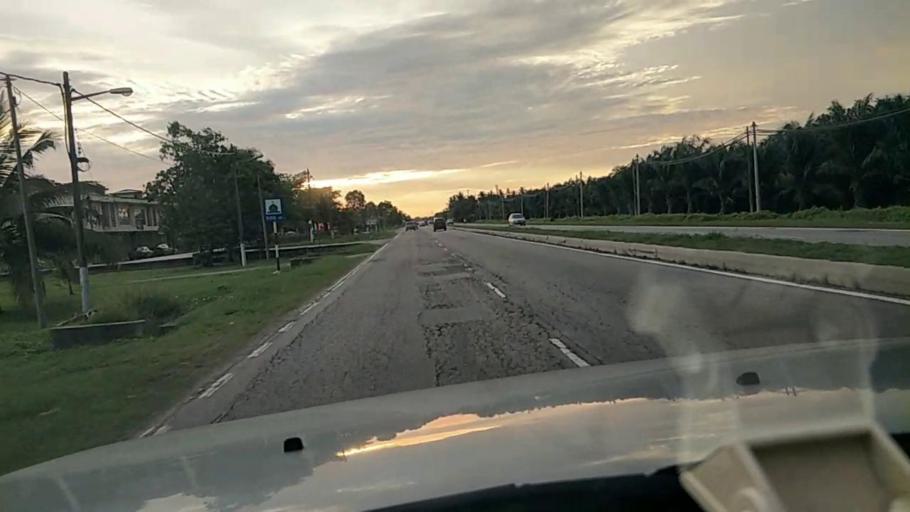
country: MY
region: Perak
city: Kampong Dungun
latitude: 3.1428
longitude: 101.3589
